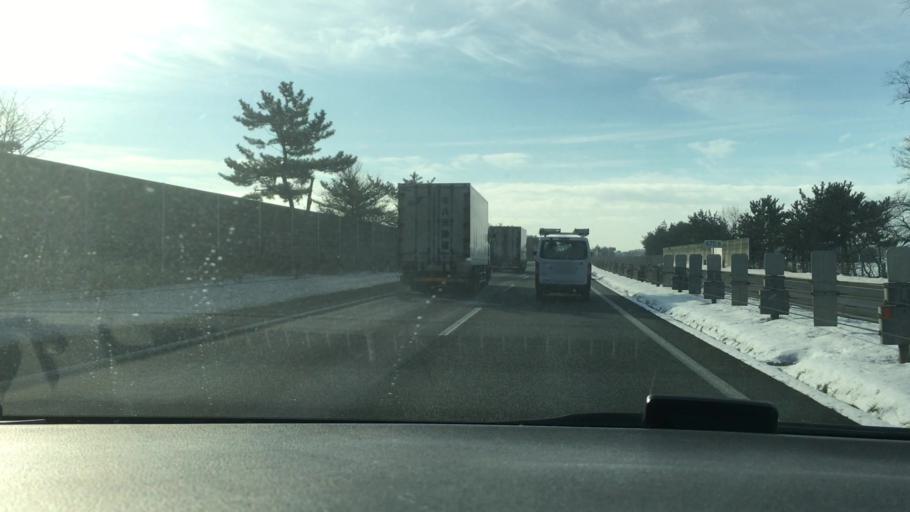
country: JP
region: Iwate
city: Hanamaki
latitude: 39.3972
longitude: 141.0926
